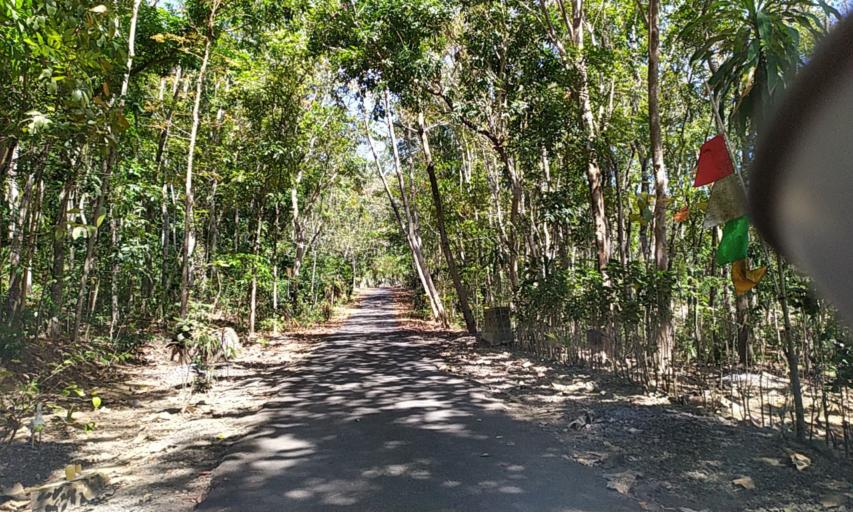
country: ID
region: Central Java
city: Adipala
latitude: -7.6807
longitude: 109.1844
